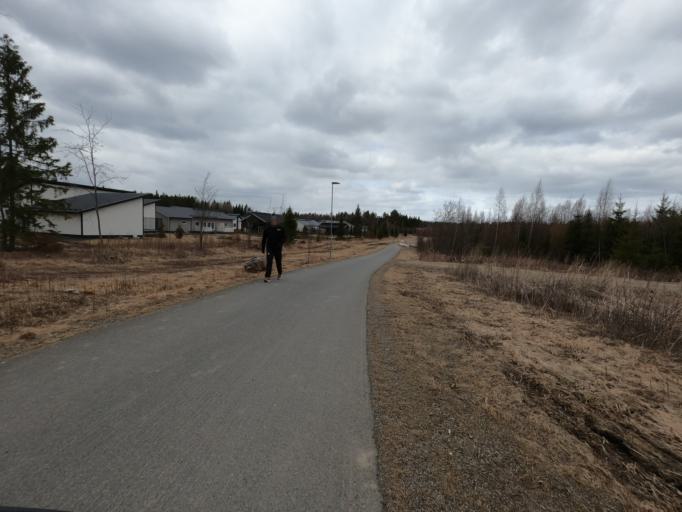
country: FI
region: North Karelia
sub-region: Joensuu
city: Joensuu
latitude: 62.5662
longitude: 29.8183
